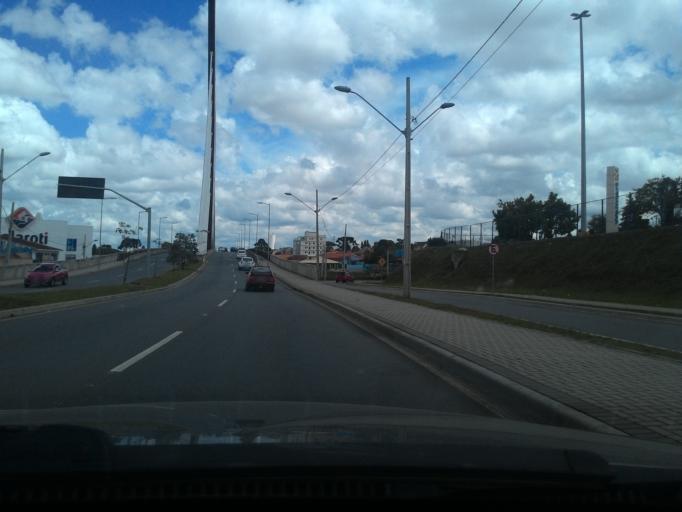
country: BR
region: Parana
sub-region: Pinhais
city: Pinhais
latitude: -25.4664
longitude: -49.2318
